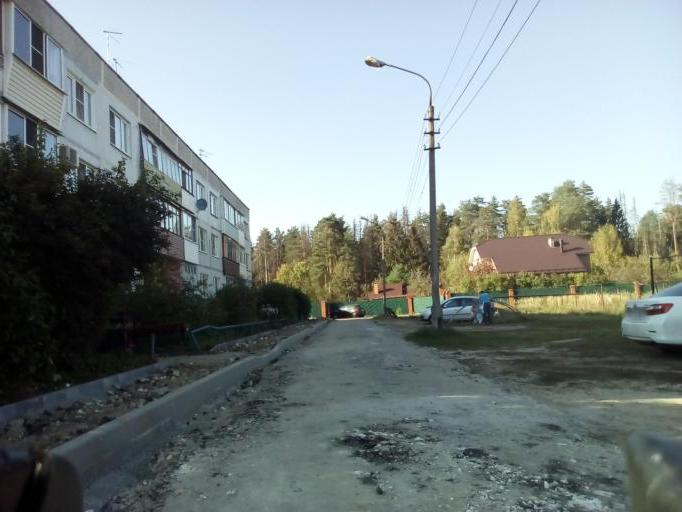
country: RU
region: Moskovskaya
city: Malyshevo
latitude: 55.5581
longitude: 38.3218
